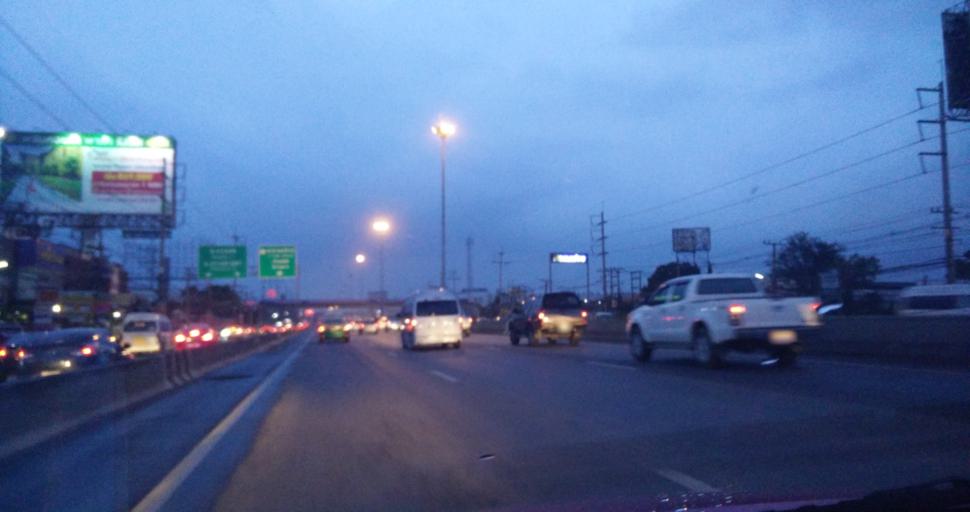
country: TH
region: Pathum Thani
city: Khlong Luang
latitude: 14.0284
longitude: 100.6158
